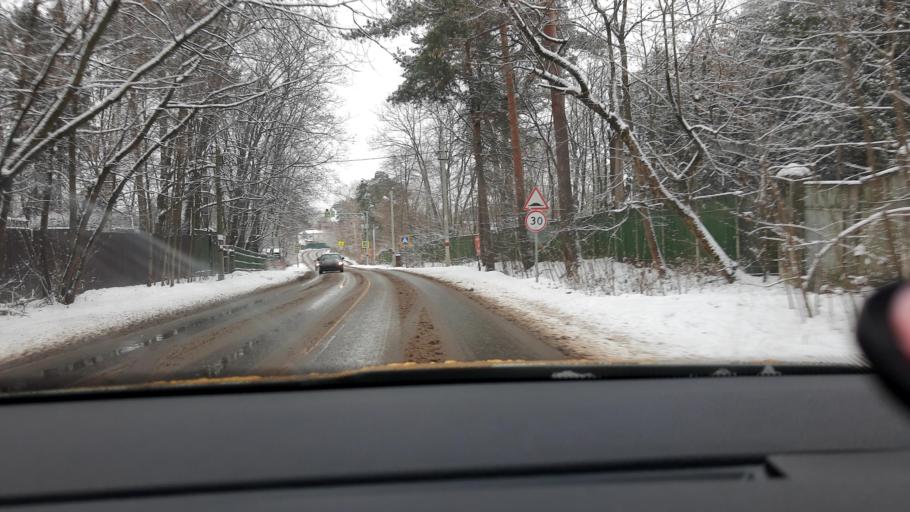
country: RU
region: Moskovskaya
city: Mamontovka
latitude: 55.9729
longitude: 37.8235
